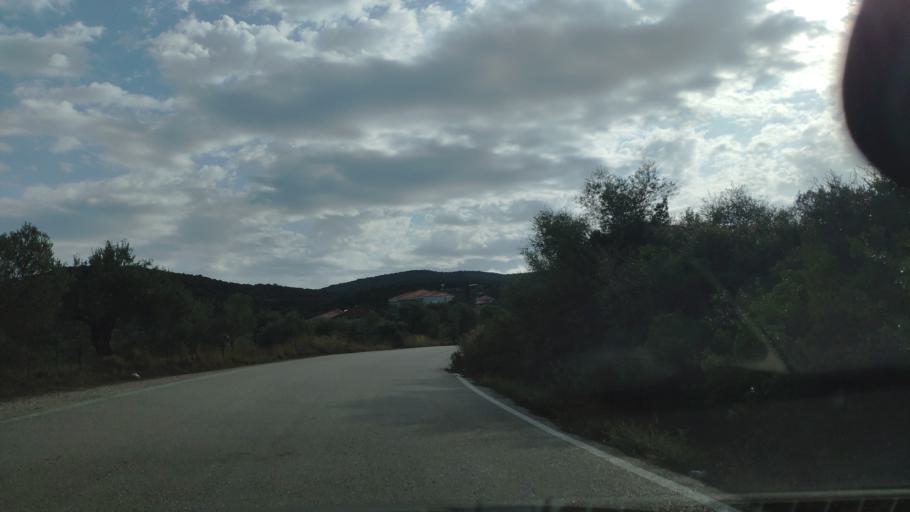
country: GR
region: West Greece
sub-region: Nomos Aitolias kai Akarnanias
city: Sardinia
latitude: 38.8905
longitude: 21.2220
